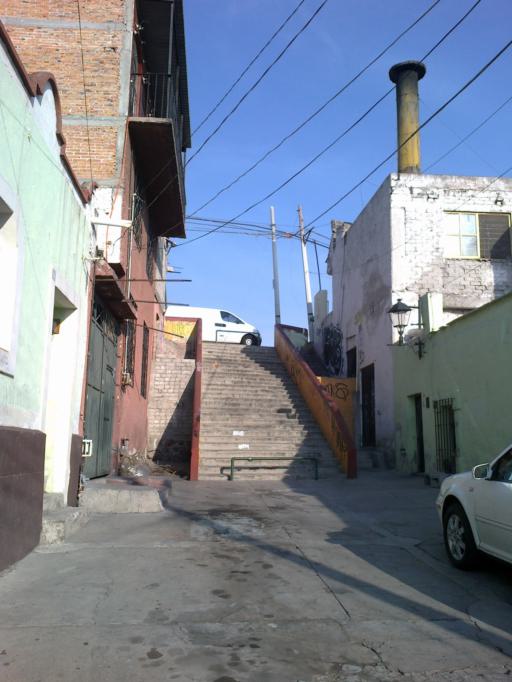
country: MX
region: Queretaro
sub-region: Queretaro
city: Santiago de Queretaro
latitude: 20.6019
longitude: -100.3941
